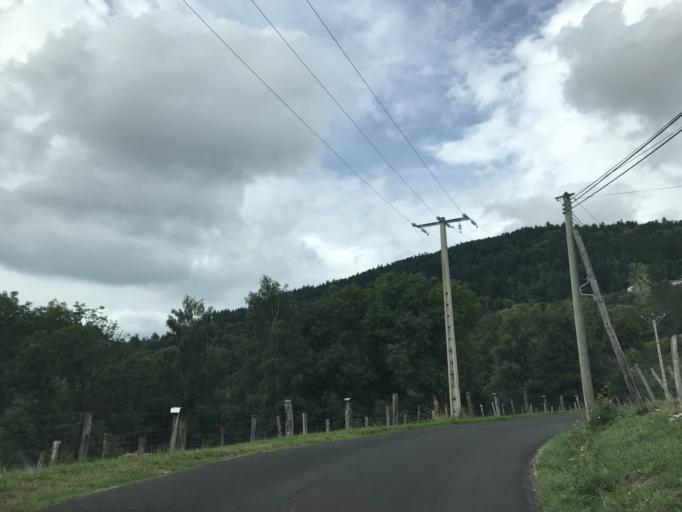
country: FR
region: Auvergne
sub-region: Departement du Puy-de-Dome
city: Job
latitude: 45.6692
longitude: 3.7560
